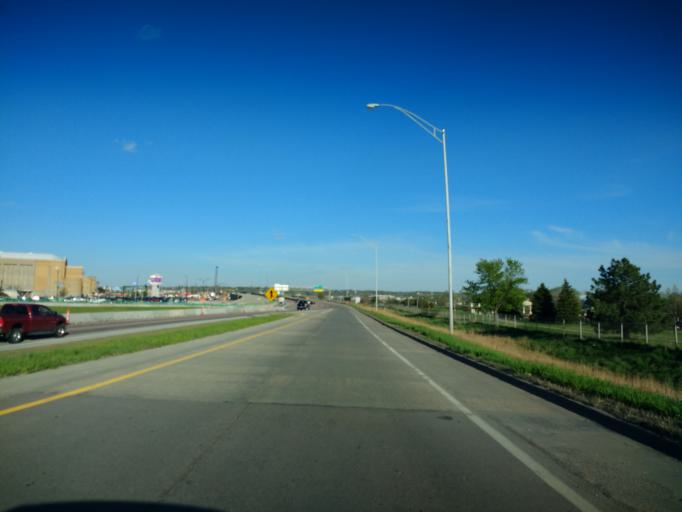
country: US
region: Iowa
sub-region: Woodbury County
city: Sioux City
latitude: 42.4905
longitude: -96.4108
